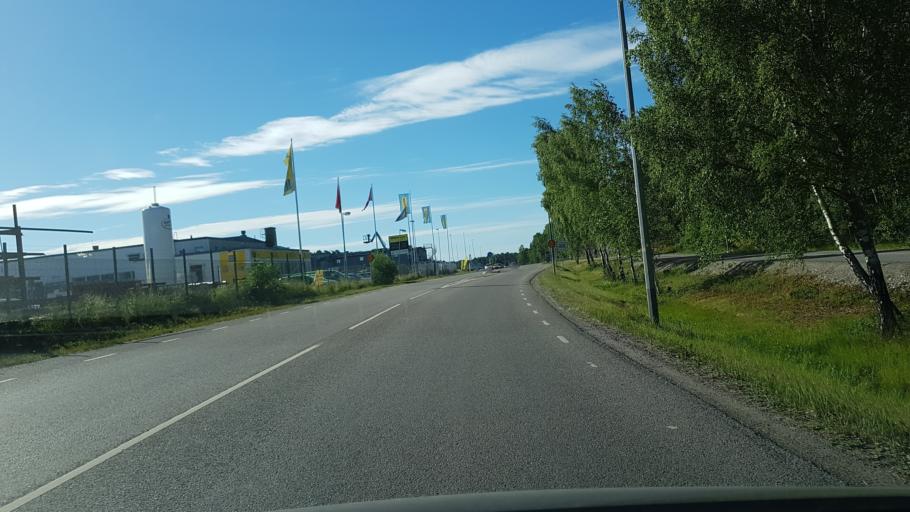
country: SE
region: Stockholm
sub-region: Jarfalla Kommun
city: Jakobsberg
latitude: 59.4090
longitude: 17.8377
